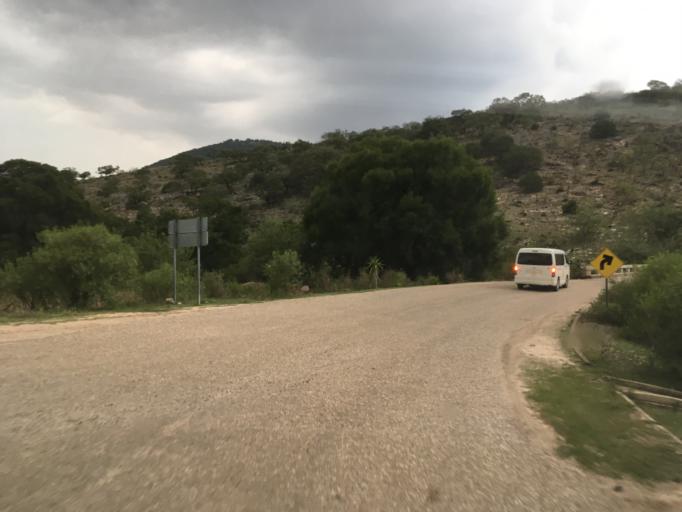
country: MX
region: Oaxaca
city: Santiago Tilantongo
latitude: 17.2602
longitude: -97.3116
